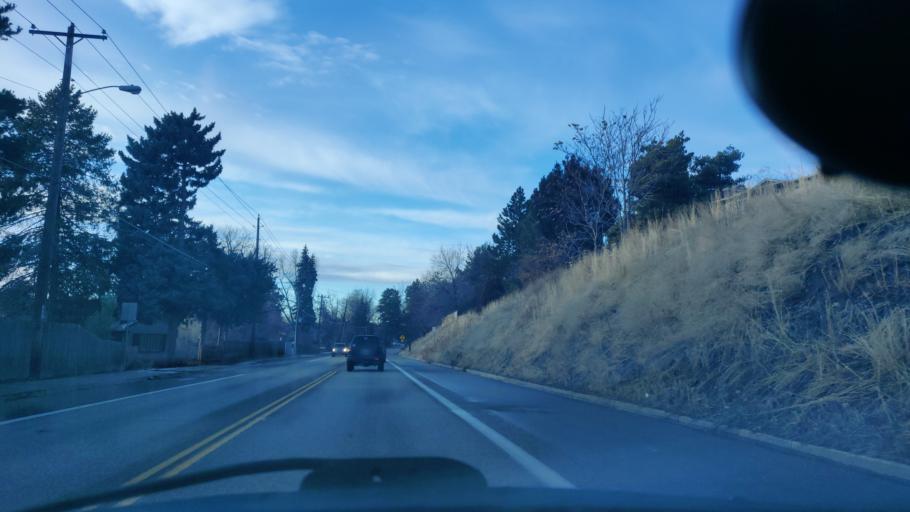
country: US
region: Idaho
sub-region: Ada County
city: Boise
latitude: 43.6419
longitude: -116.2116
